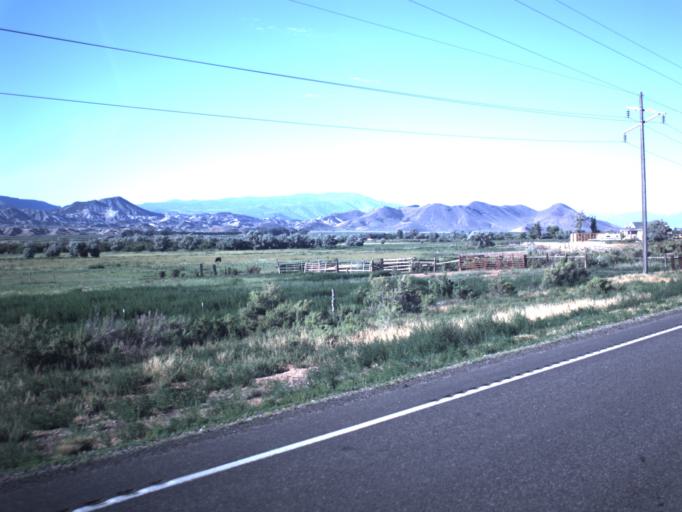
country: US
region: Utah
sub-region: Sevier County
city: Aurora
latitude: 38.9337
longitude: -111.8986
